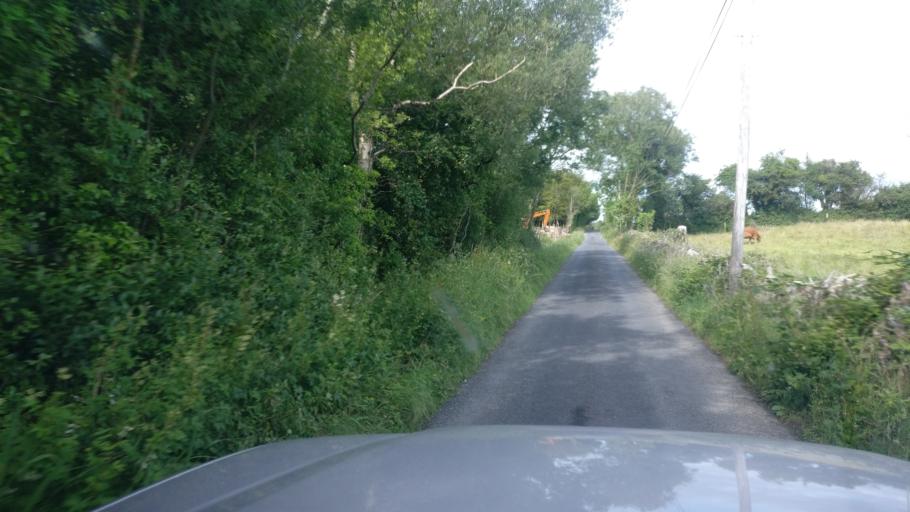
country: IE
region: Connaught
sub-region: County Galway
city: Gort
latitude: 53.1022
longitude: -8.7155
